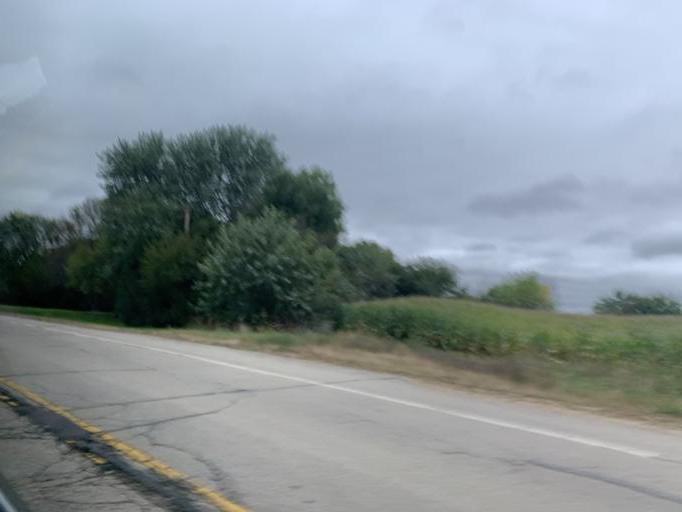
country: US
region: Wisconsin
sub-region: Grant County
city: Muscoda
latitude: 43.2144
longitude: -90.4640
